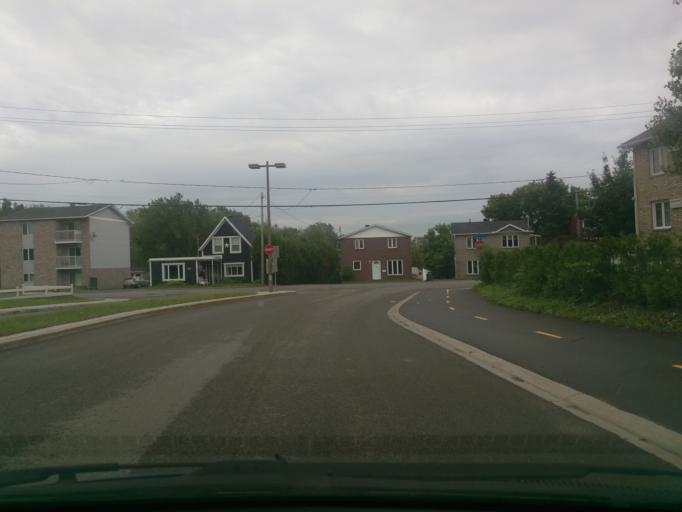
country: CA
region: Quebec
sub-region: Outaouais
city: Gatineau
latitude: 45.4730
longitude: -75.6770
